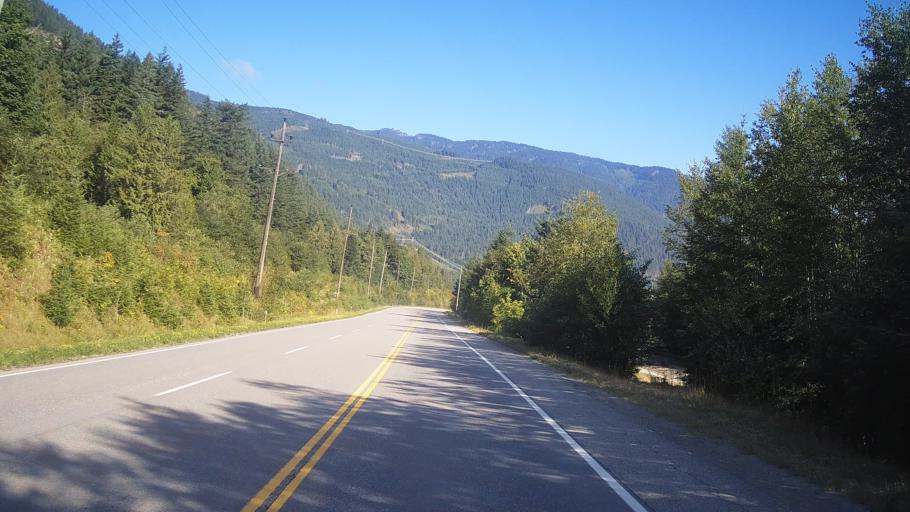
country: CA
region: British Columbia
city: Hope
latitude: 49.5330
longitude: -121.4262
